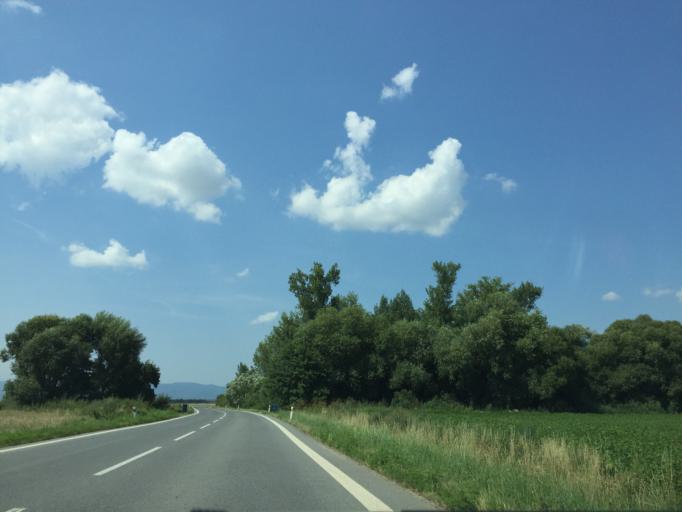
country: SK
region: Kosicky
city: Sobrance
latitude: 48.7238
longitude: 22.2141
